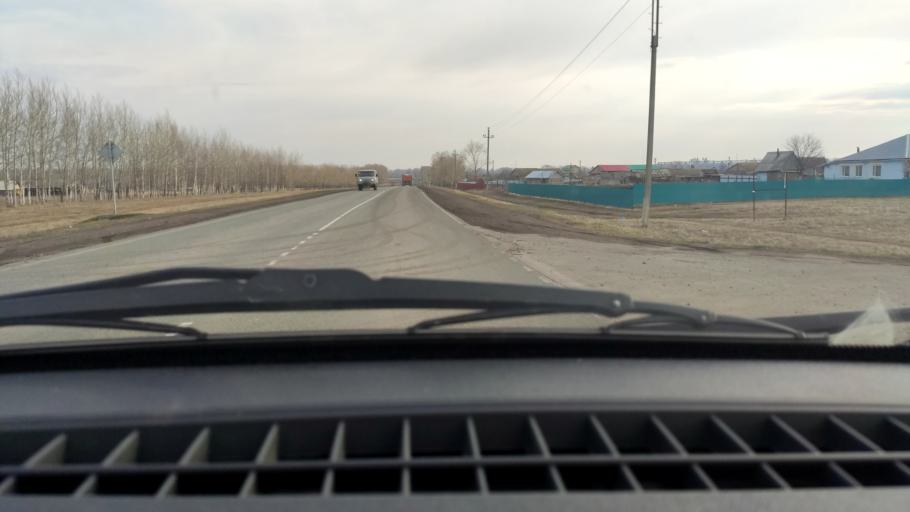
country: RU
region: Bashkortostan
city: Davlekanovo
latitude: 54.3859
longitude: 55.1983
